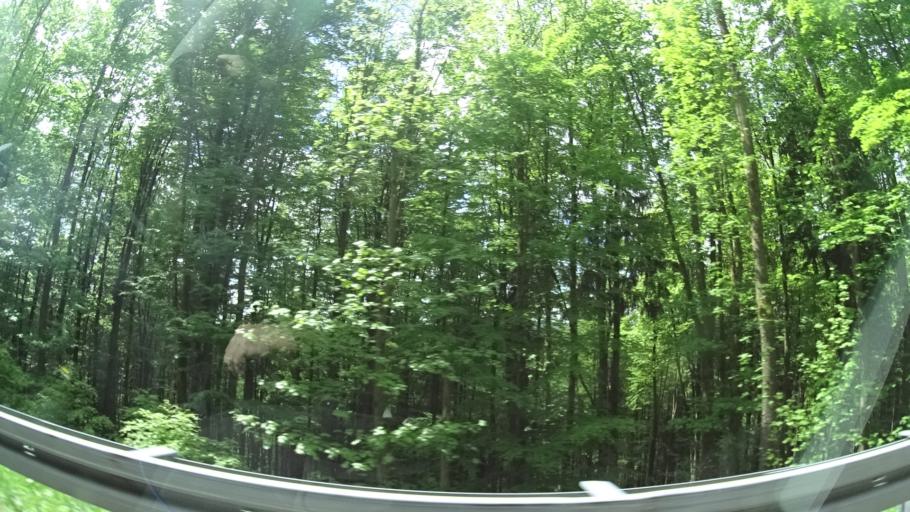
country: DE
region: Thuringia
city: Schmiedefeld am Rennsteig
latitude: 50.6126
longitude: 10.7842
